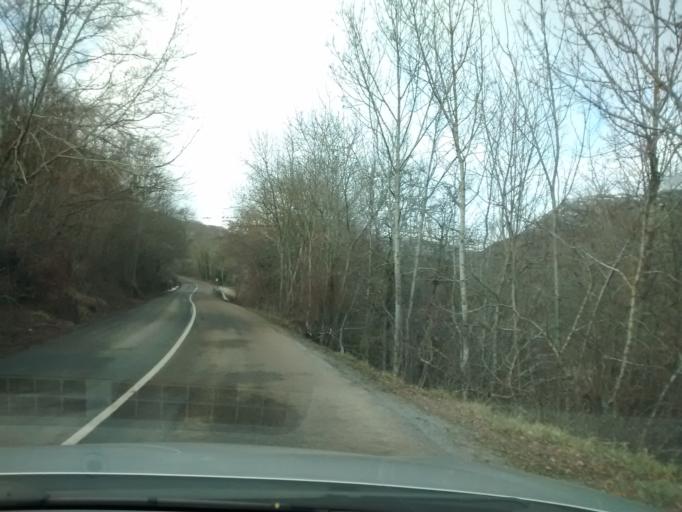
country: ES
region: Castille and Leon
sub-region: Provincia de Burgos
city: Espinosa de los Monteros
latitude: 43.1212
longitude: -3.6014
